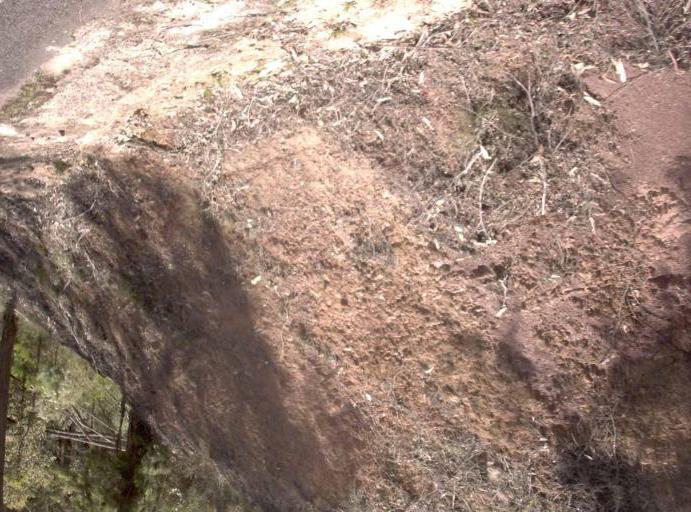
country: AU
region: New South Wales
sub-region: Bombala
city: Bombala
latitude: -37.6155
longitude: 148.8897
